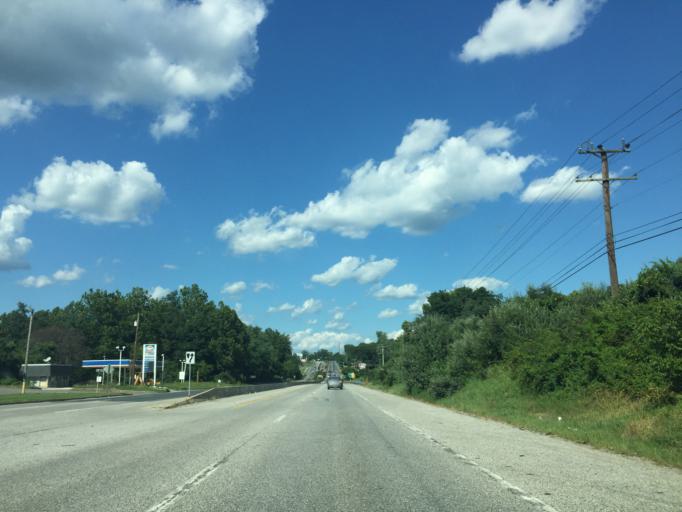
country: US
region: Maryland
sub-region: Harford County
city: Joppatowne
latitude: 39.4196
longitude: -76.3758
